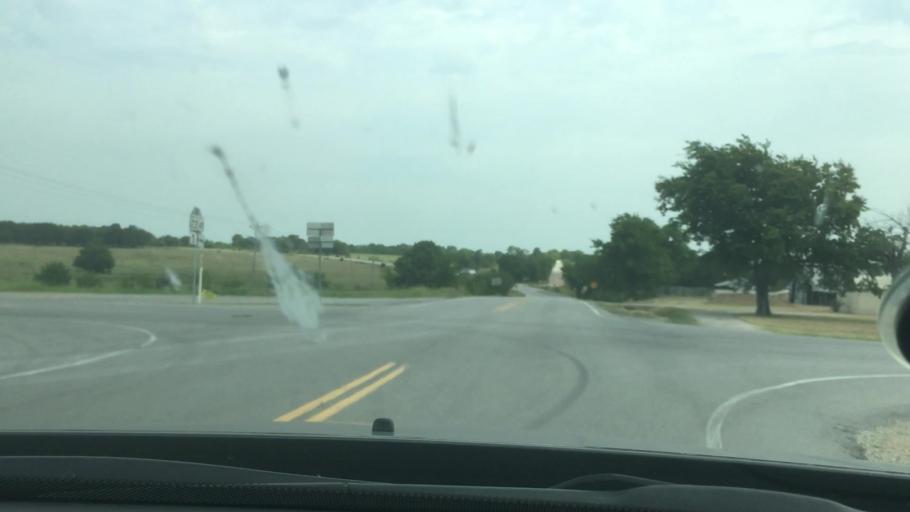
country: US
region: Oklahoma
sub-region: Bryan County
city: Durant
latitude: 34.1425
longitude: -96.3732
